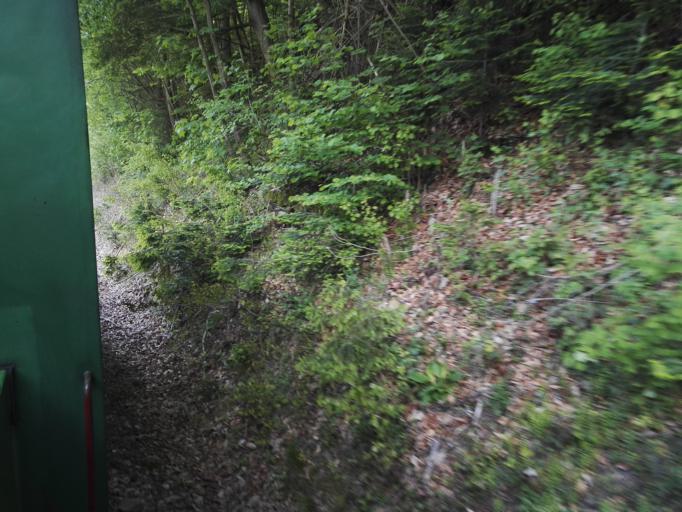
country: AT
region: Styria
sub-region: Politischer Bezirk Weiz
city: Koglhof
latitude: 47.3059
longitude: 15.6952
